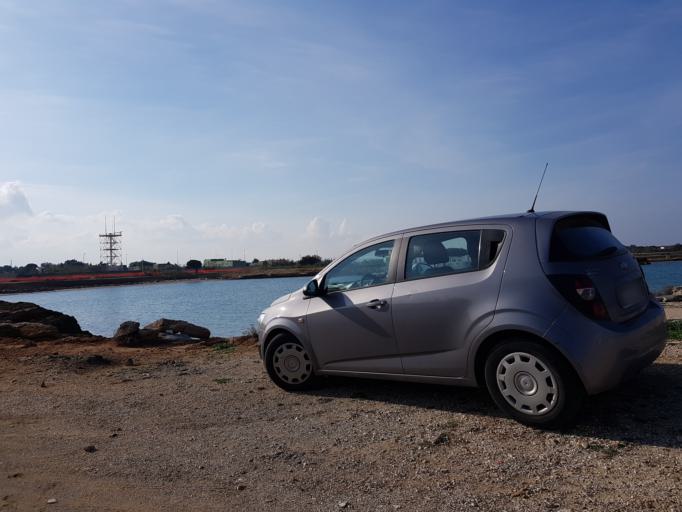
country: IT
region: Apulia
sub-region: Provincia di Brindisi
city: Materdomini
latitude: 40.6611
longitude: 17.9599
